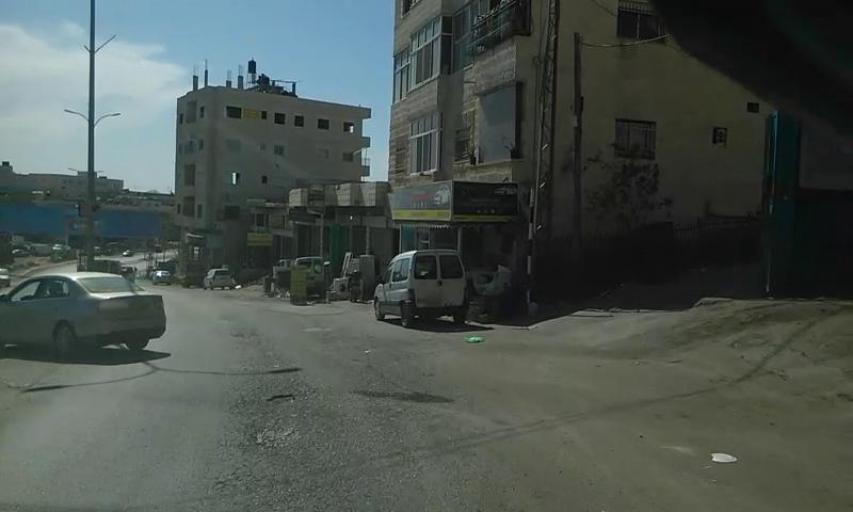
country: PS
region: West Bank
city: Al `Ayzariyah
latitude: 31.7595
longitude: 35.2815
